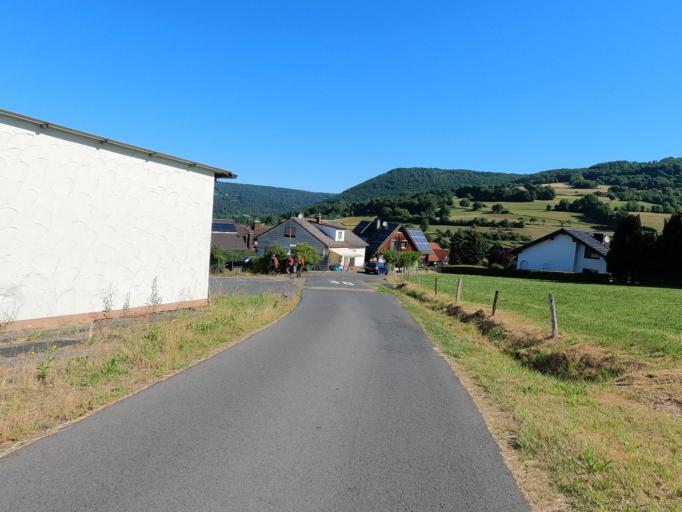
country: DE
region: Bavaria
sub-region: Regierungsbezirk Unterfranken
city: Zeitlofs
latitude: 50.3093
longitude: 9.6718
